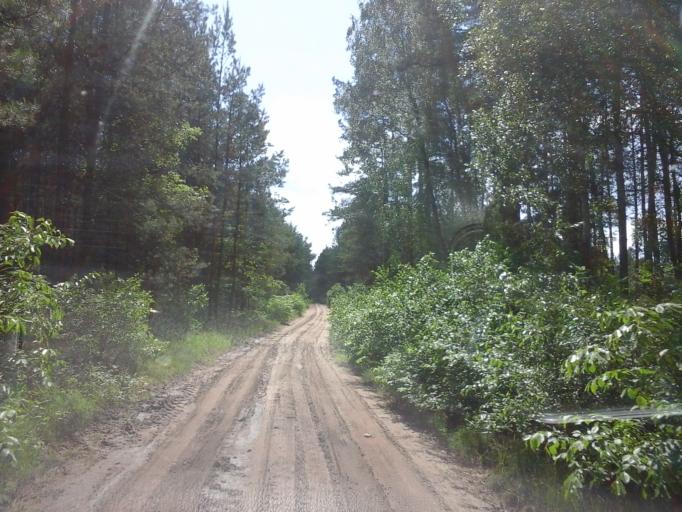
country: PL
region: West Pomeranian Voivodeship
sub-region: Powiat choszczenski
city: Bierzwnik
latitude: 53.1275
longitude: 15.6666
